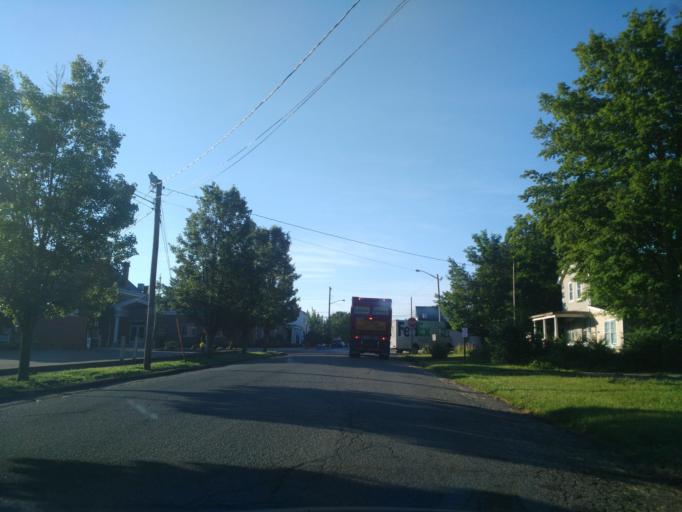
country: US
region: Ohio
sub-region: Pike County
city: Waverly
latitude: 39.1257
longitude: -82.9861
